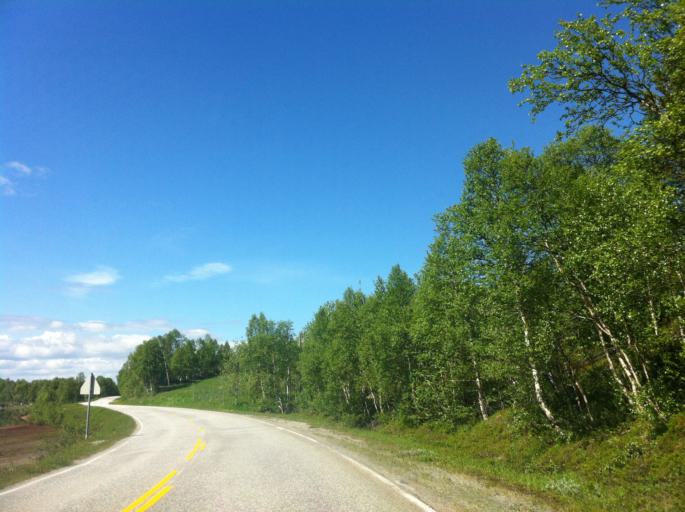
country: NO
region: Sor-Trondelag
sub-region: Roros
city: Roros
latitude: 62.5994
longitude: 11.5295
